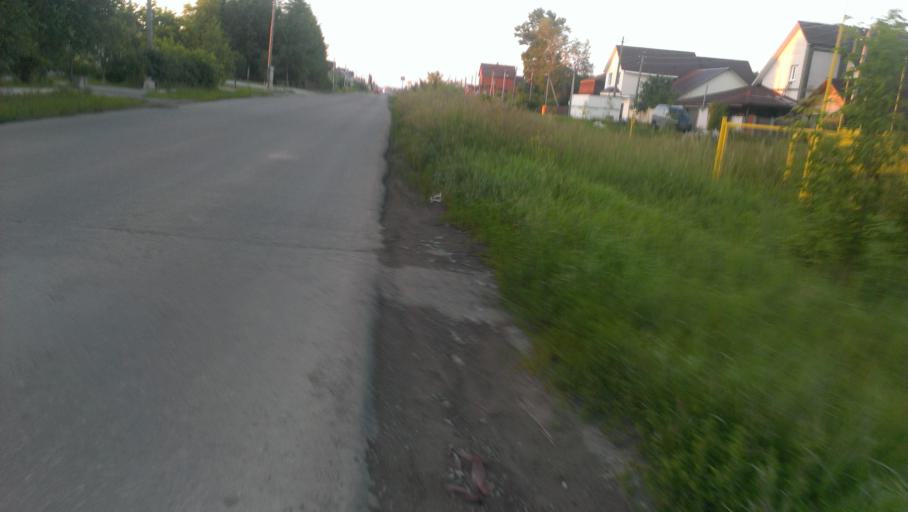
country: RU
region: Altai Krai
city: Novosilikatnyy
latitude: 53.3636
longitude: 83.6442
